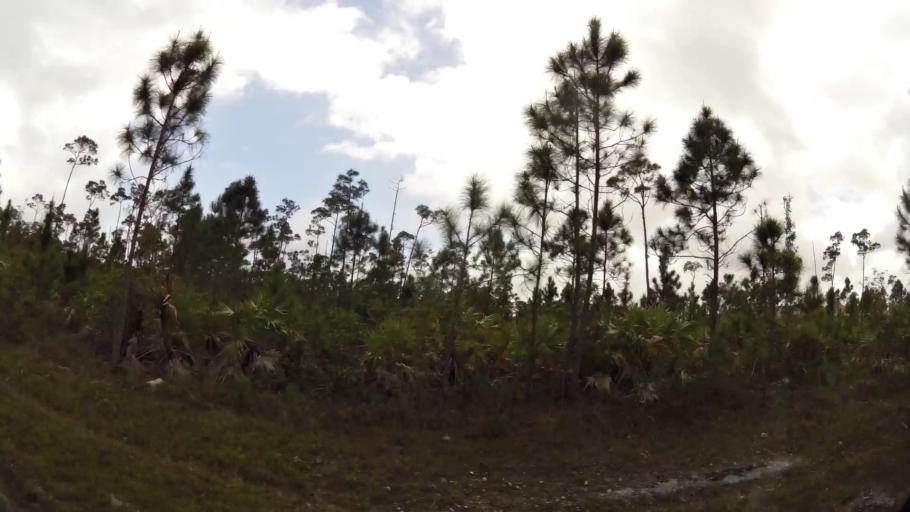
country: BS
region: Freeport
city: Lucaya
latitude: 26.5585
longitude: -78.5768
